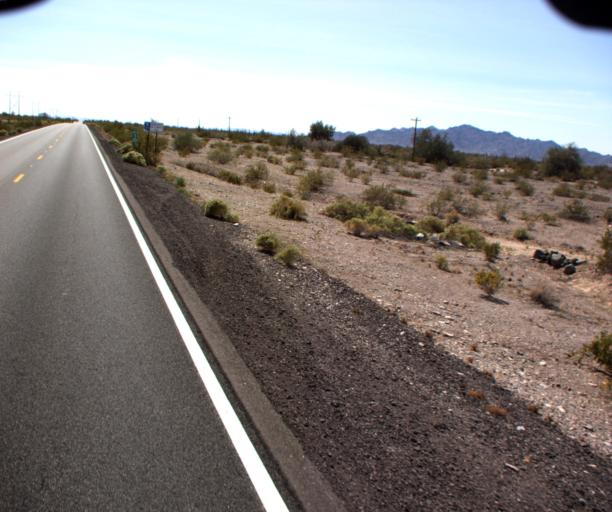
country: US
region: Arizona
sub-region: La Paz County
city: Quartzsite
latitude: 33.6017
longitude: -114.2171
